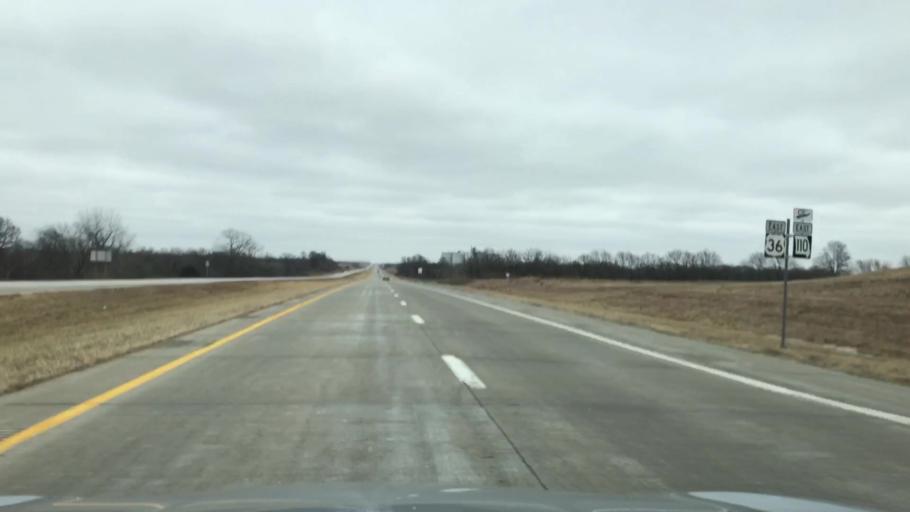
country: US
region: Missouri
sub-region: Caldwell County
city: Hamilton
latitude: 39.7354
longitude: -93.9261
